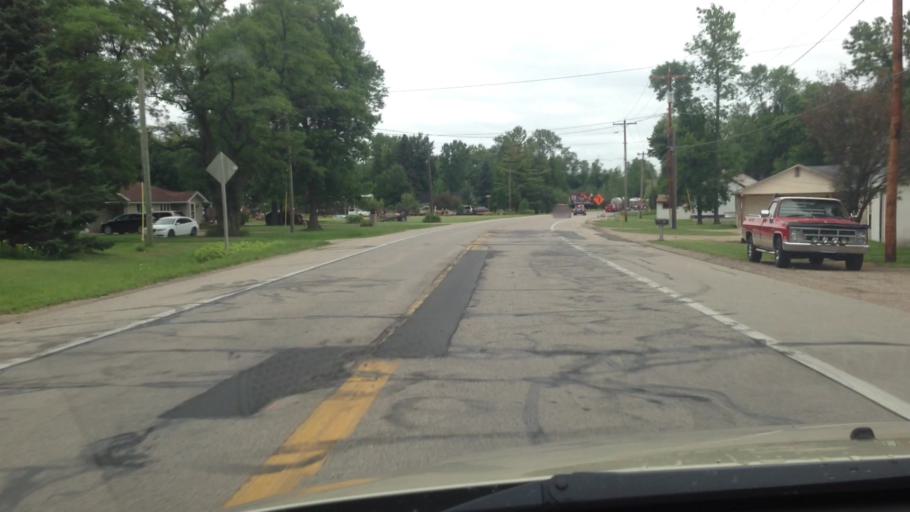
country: US
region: Michigan
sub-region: Delta County
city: Escanaba
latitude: 45.6961
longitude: -87.1011
